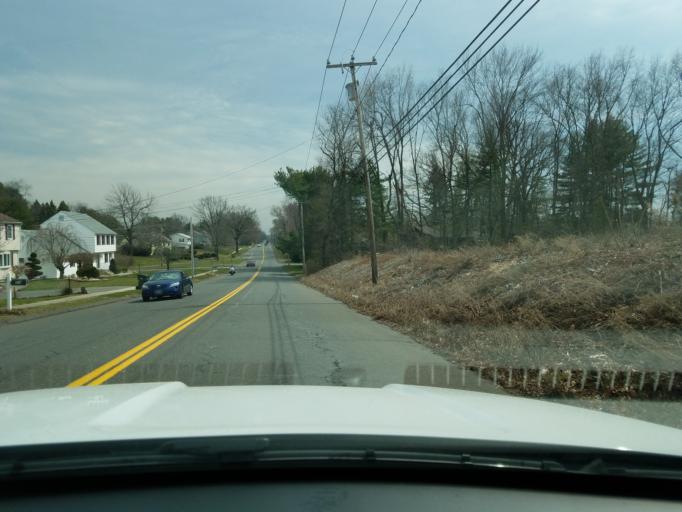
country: US
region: Connecticut
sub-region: Hartford County
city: Newington
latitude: 41.6814
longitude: -72.6908
